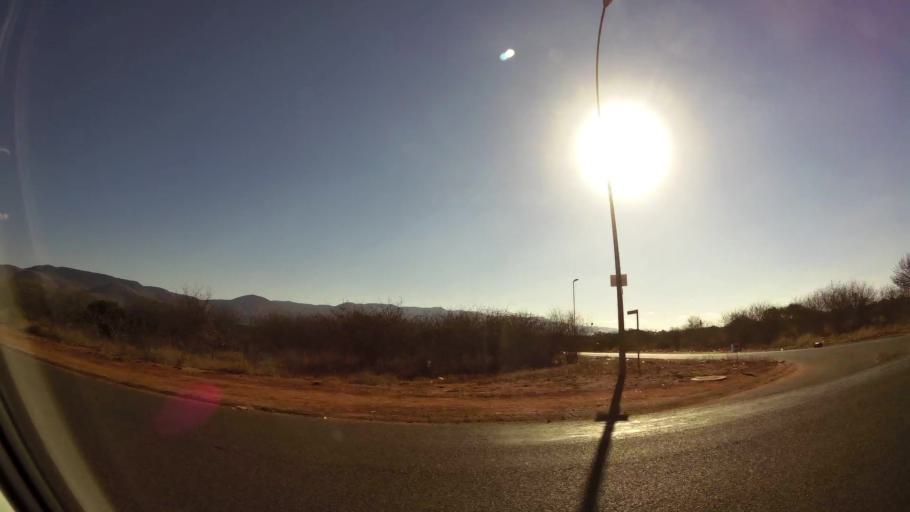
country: ZA
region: Limpopo
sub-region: Waterberg District Municipality
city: Mokopane
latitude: -24.1974
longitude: 29.0034
